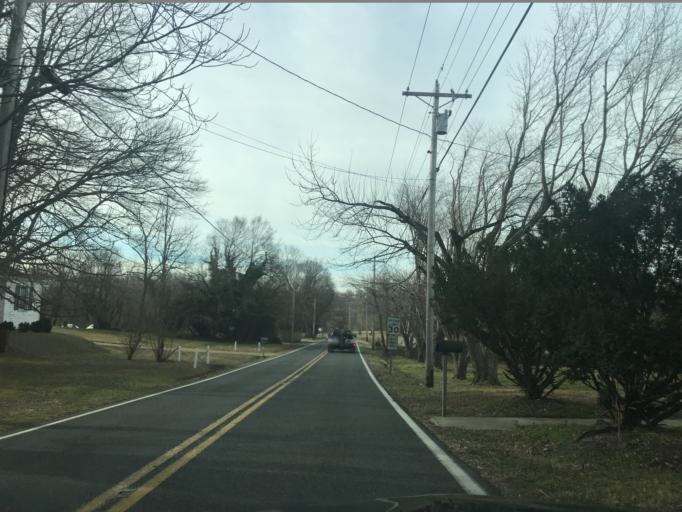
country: US
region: Maryland
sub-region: Charles County
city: Hughesville
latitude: 38.5542
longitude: -76.8425
